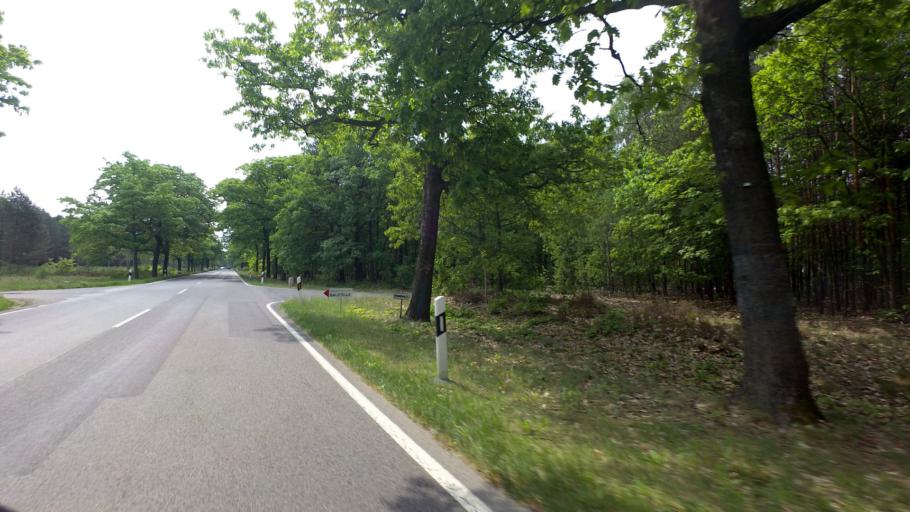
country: DE
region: Brandenburg
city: Drachhausen
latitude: 51.9213
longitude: 14.3482
